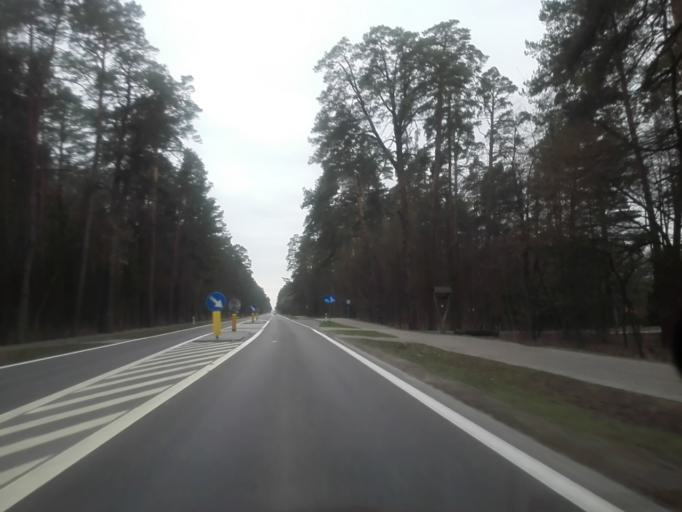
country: PL
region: Podlasie
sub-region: Powiat grajewski
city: Rajgrod
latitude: 53.7031
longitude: 22.6613
